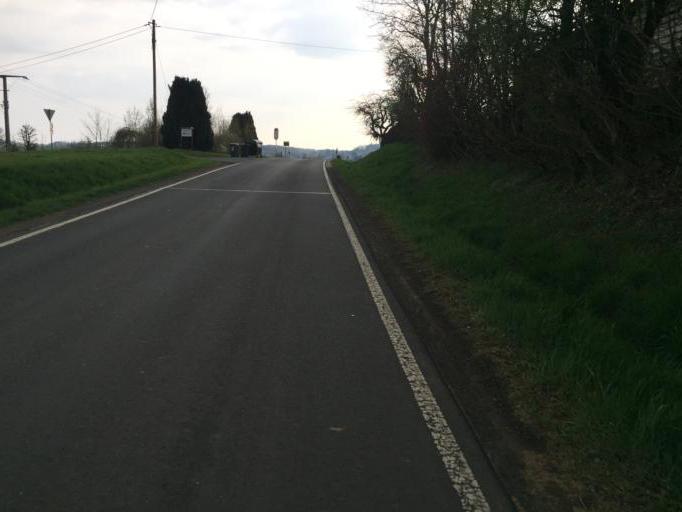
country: DE
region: Hesse
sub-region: Regierungsbezirk Giessen
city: Grunberg
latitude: 50.5605
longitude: 8.9584
